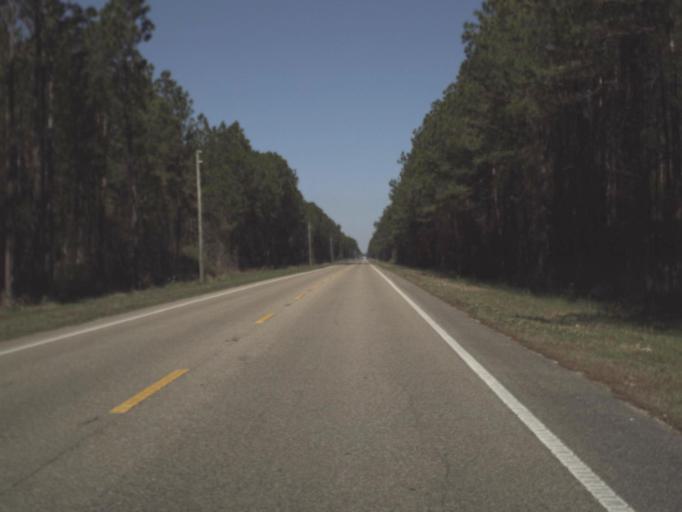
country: US
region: Florida
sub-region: Gulf County
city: Port Saint Joe
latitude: 29.8416
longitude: -85.2680
